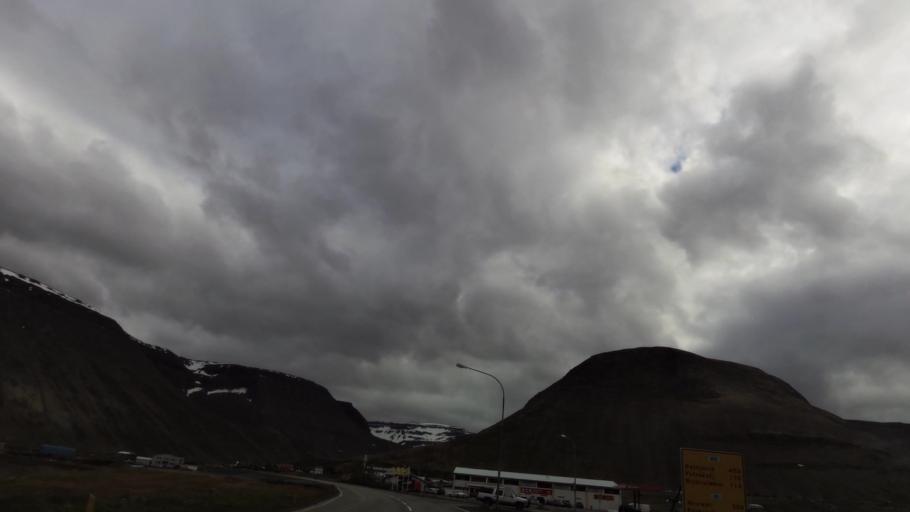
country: IS
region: Westfjords
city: Isafjoerdur
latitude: 66.0615
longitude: -23.1742
